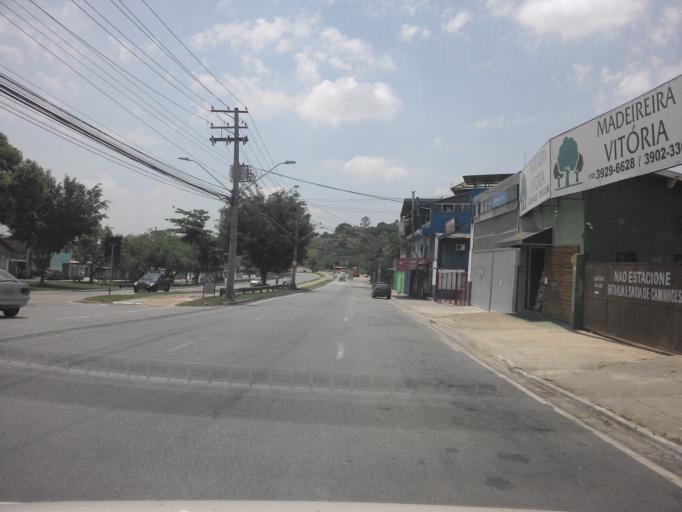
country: BR
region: Sao Paulo
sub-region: Sao Jose Dos Campos
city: Sao Jose dos Campos
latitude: -23.1699
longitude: -45.8104
